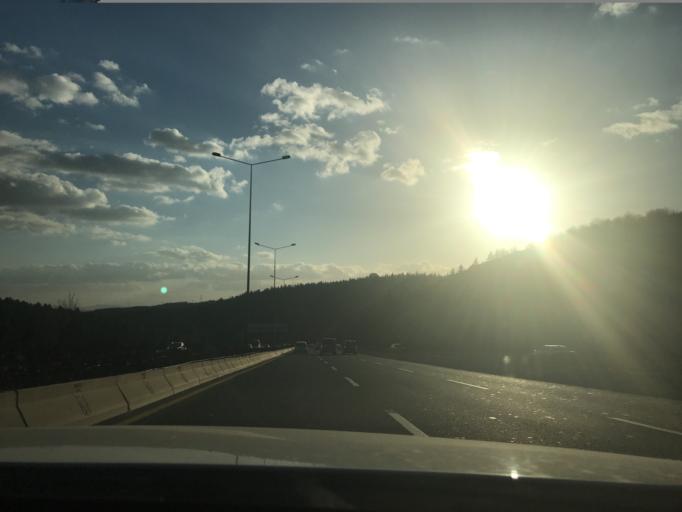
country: TR
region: Ankara
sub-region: Goelbasi
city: Golbasi
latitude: 39.8395
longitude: 32.8015
